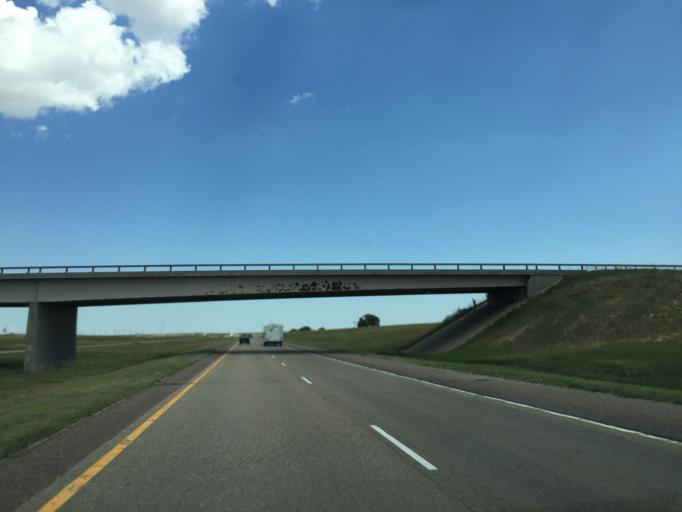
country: US
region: Colorado
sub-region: Lincoln County
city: Hugo
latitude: 39.2787
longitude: -103.3983
